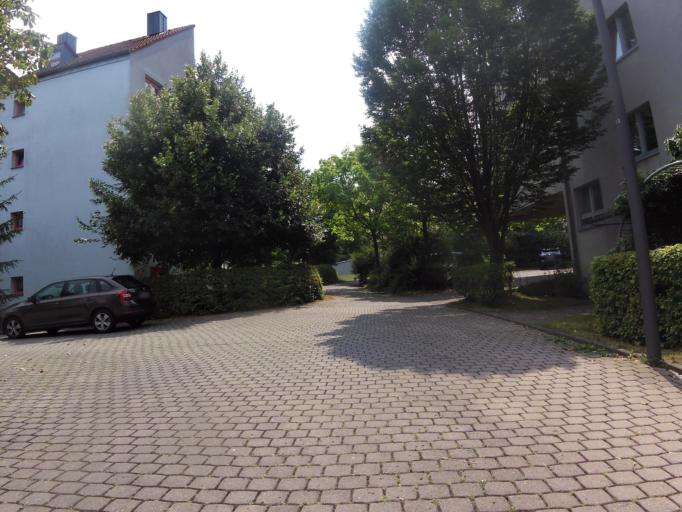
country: DE
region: Bavaria
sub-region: Regierungsbezirk Unterfranken
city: Randersacker
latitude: 49.7392
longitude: 9.9630
